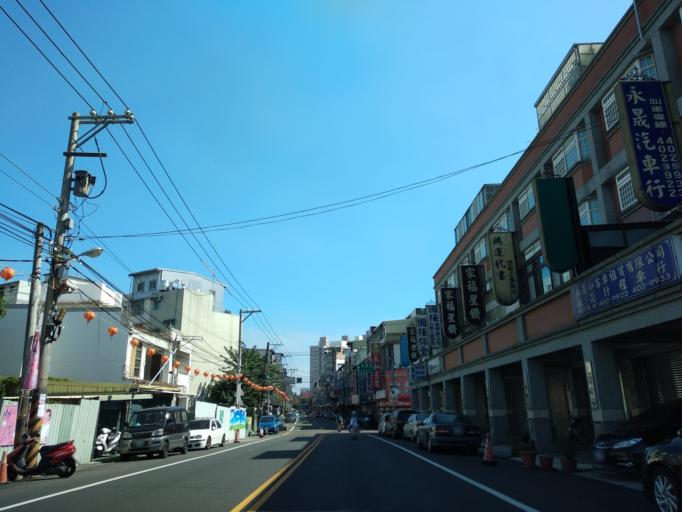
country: TW
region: Taiwan
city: Taoyuan City
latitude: 24.9469
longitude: 121.2114
